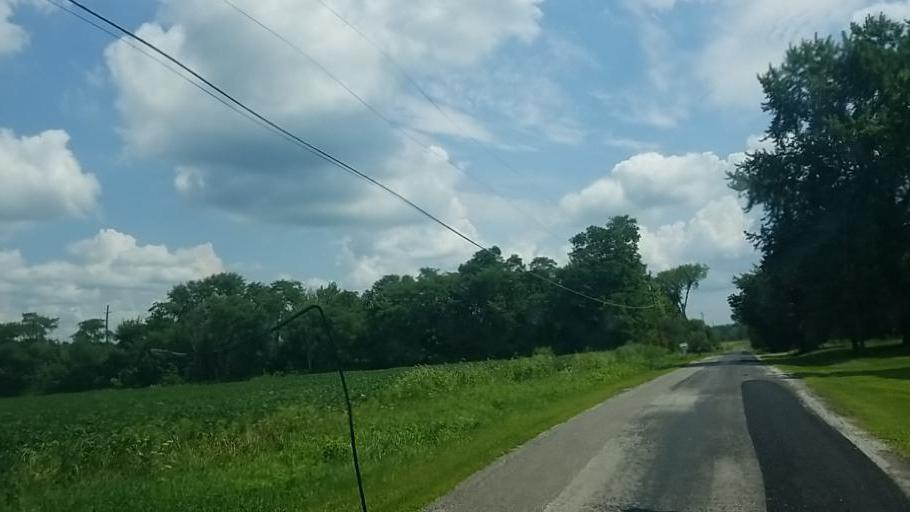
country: US
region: Ohio
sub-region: Wayne County
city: West Salem
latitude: 41.0296
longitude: -82.0897
